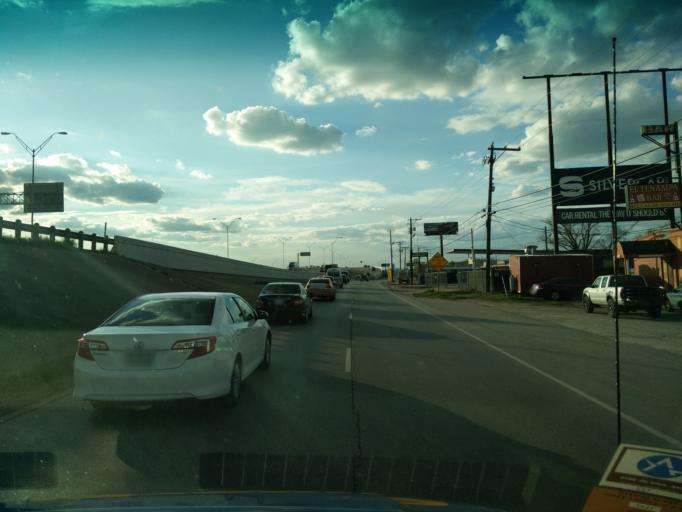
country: US
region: Texas
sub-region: Travis County
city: Hornsby Bend
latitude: 30.2139
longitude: -97.6600
